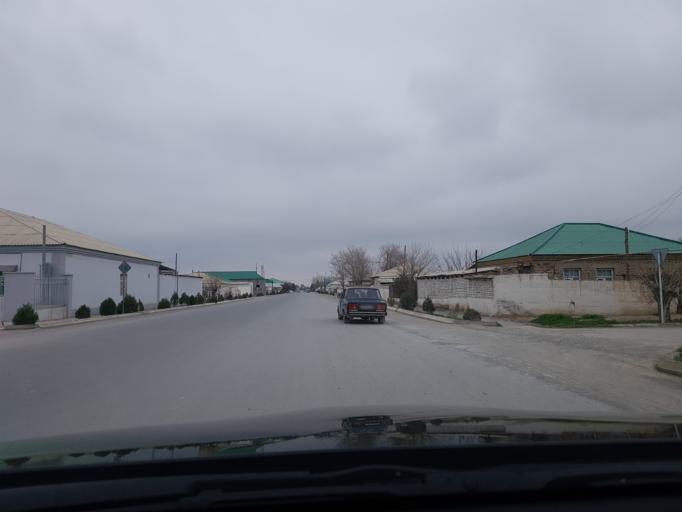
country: TM
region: Ahal
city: Abadan
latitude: 38.1497
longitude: 57.9564
